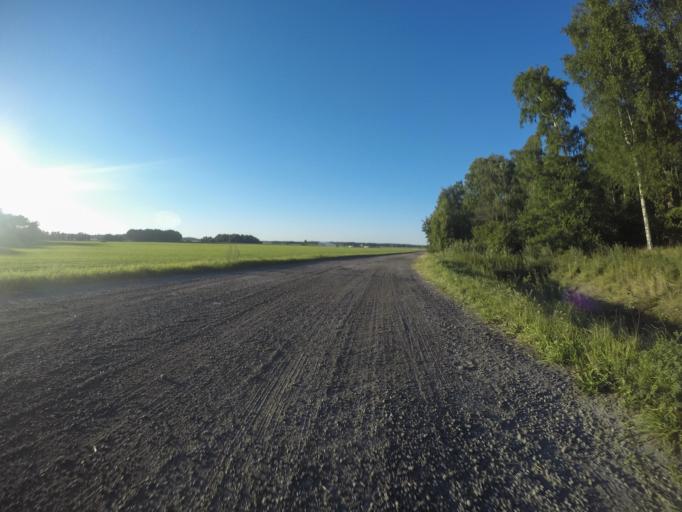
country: SE
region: Vaestmanland
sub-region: Vasteras
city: Vasteras
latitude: 59.5735
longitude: 16.6526
